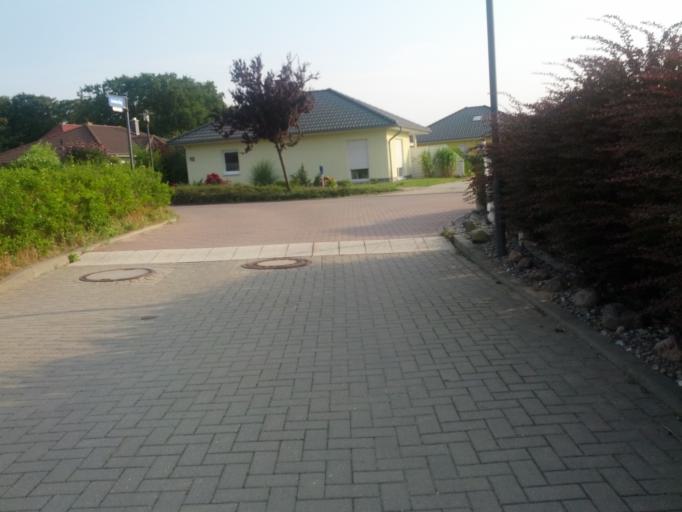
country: DE
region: Mecklenburg-Vorpommern
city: Ostseebad Kuhlungsborn
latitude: 54.1436
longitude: 11.7319
